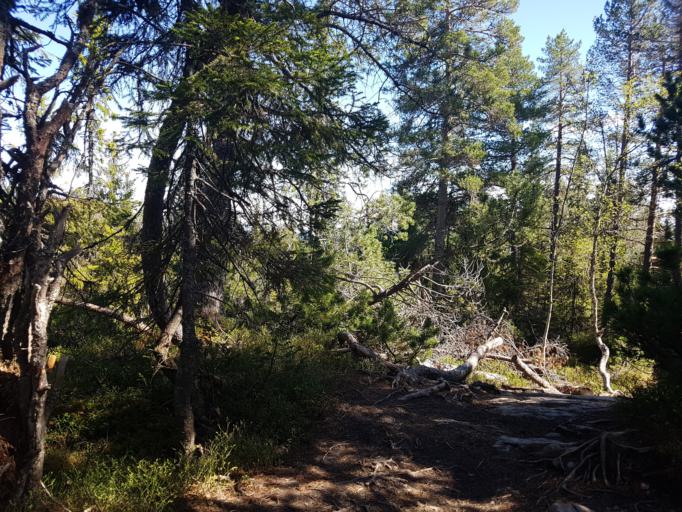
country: NO
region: Sor-Trondelag
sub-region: Trondheim
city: Trondheim
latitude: 63.4295
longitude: 10.3119
